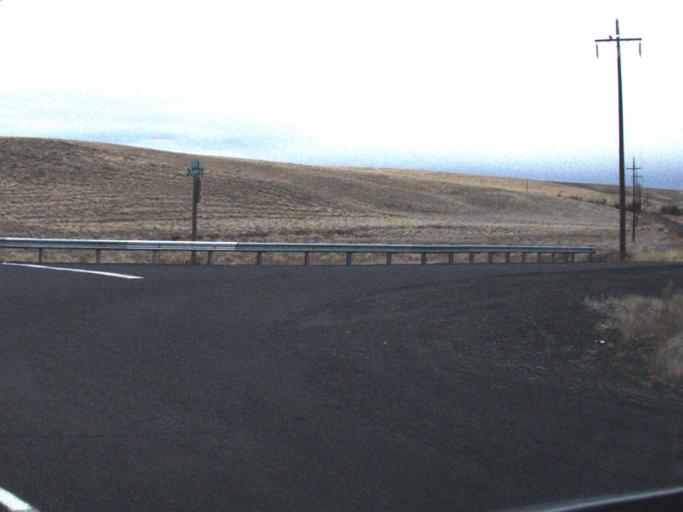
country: US
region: Washington
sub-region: Adams County
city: Ritzville
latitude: 46.7741
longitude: -118.3592
